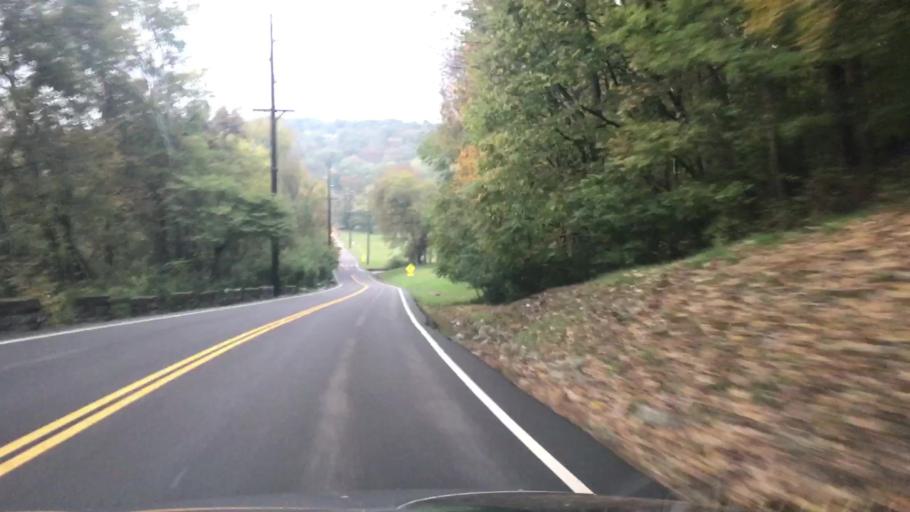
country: US
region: Tennessee
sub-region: Davidson County
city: Belle Meade
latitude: 36.0587
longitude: -86.9026
